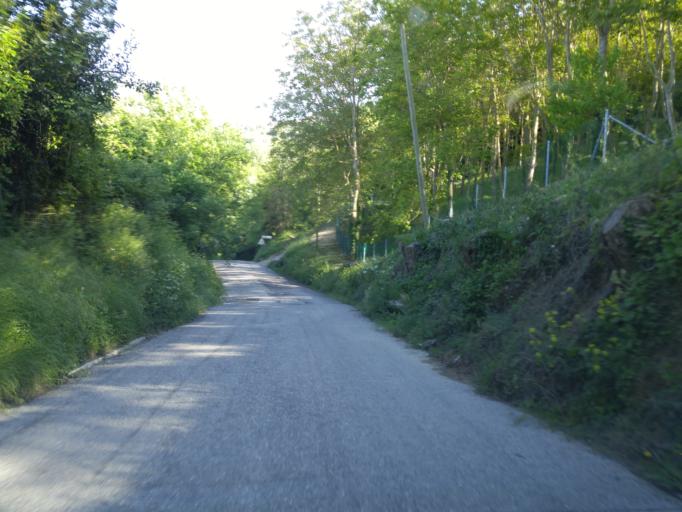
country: IT
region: The Marches
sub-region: Provincia di Pesaro e Urbino
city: Mombaroccio
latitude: 43.8087
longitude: 12.8500
